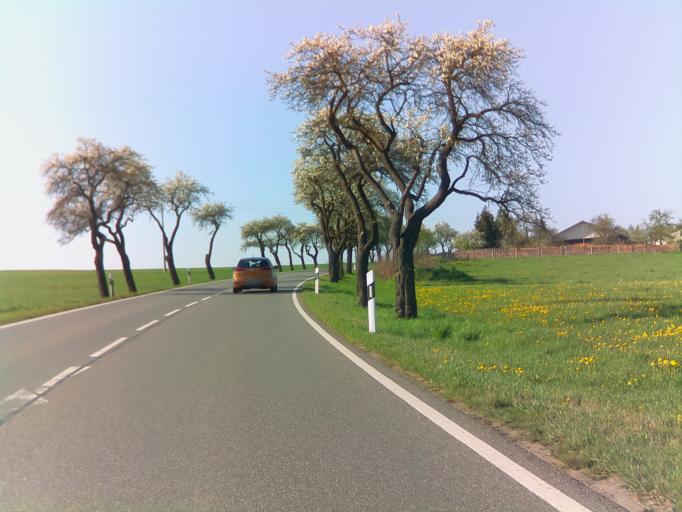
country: DE
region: Thuringia
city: Oettersdorf
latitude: 50.6002
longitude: 11.8248
